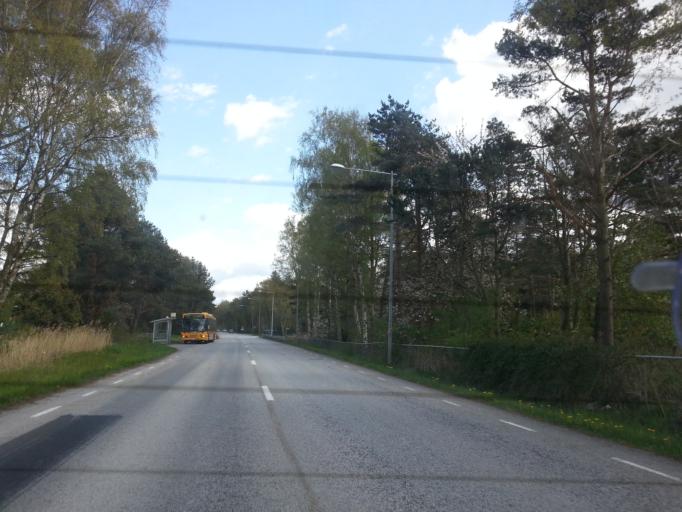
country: SE
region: Skane
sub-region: Ystads Kommun
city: Kopingebro
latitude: 55.4325
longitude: 13.9456
